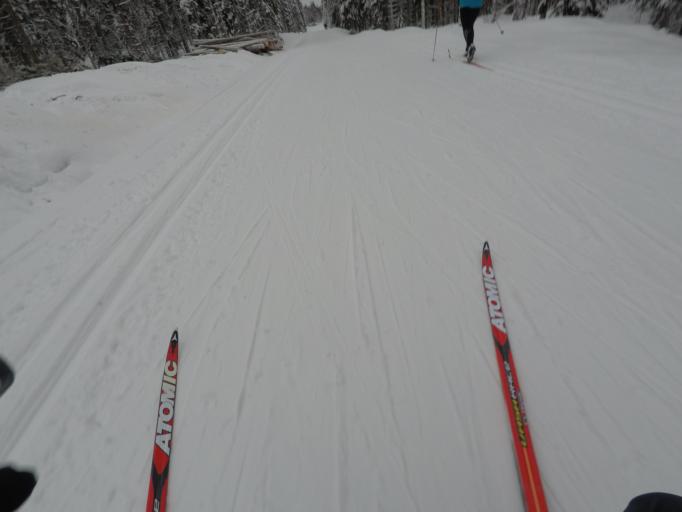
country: SE
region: Dalarna
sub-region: Ludvika Kommun
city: Abborrberget
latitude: 60.1579
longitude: 14.4893
